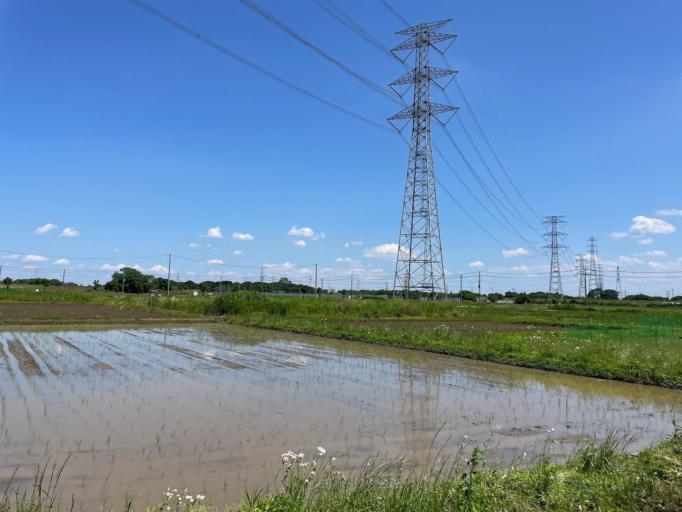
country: JP
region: Saitama
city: Sakado
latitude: 35.9999
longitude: 139.4158
